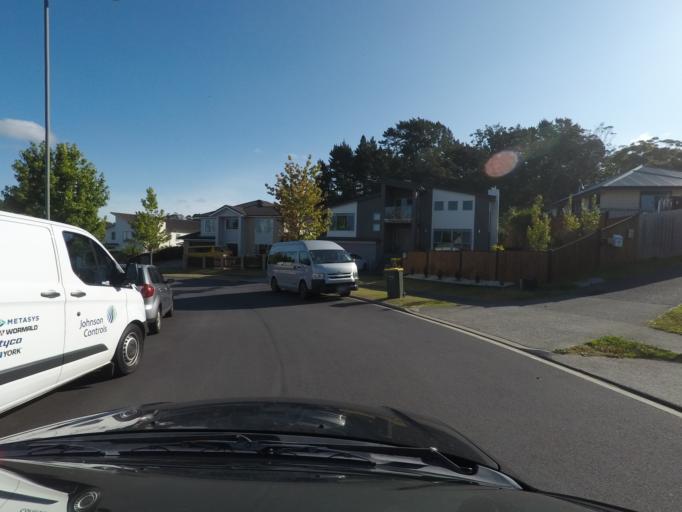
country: NZ
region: Auckland
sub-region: Auckland
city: Waitakere
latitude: -36.8823
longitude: 174.6023
